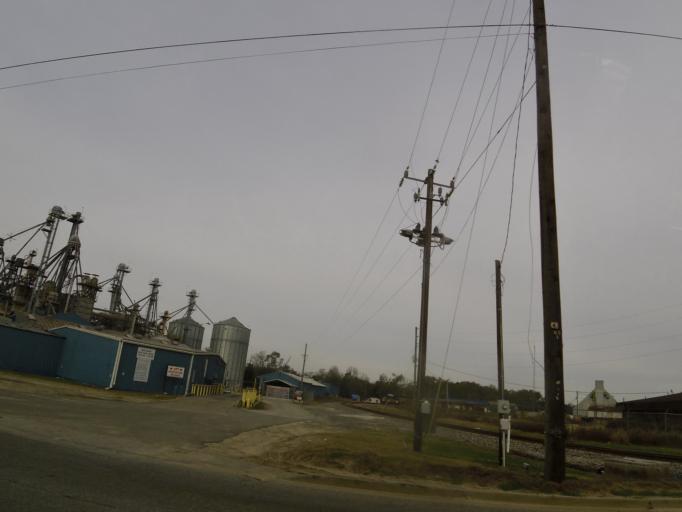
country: US
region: Georgia
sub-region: Decatur County
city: Bainbridge
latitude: 30.9149
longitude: -84.5877
